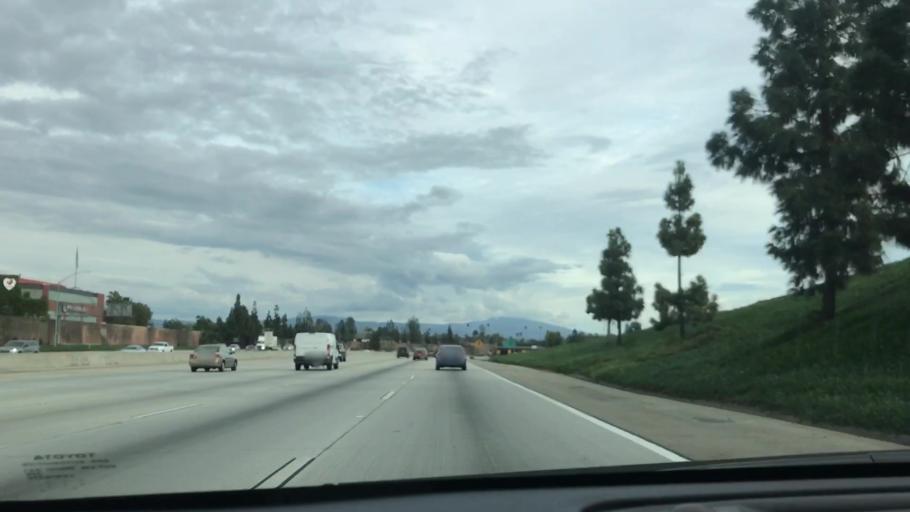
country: US
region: California
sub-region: Orange County
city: Anaheim
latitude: 33.8346
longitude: -117.9388
